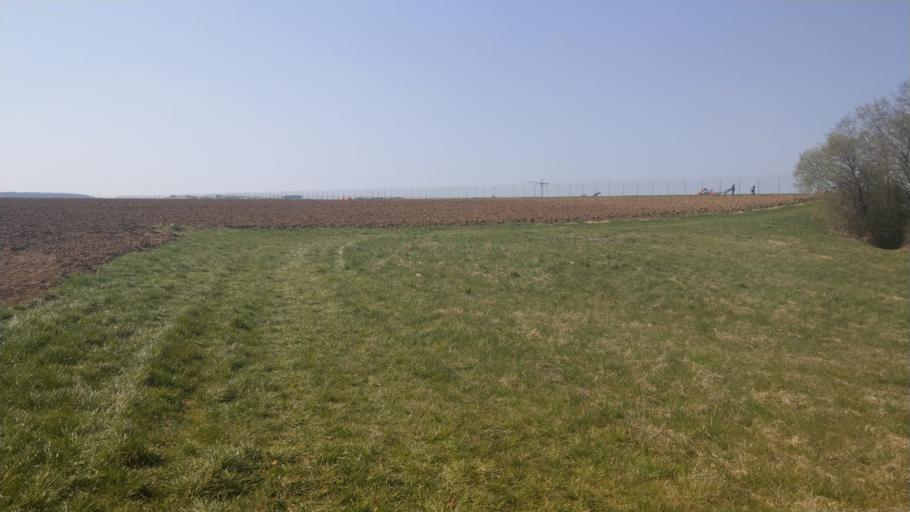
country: DE
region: Baden-Wuerttemberg
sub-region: Regierungsbezirk Stuttgart
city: Filderstadt
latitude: 48.6893
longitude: 9.2327
